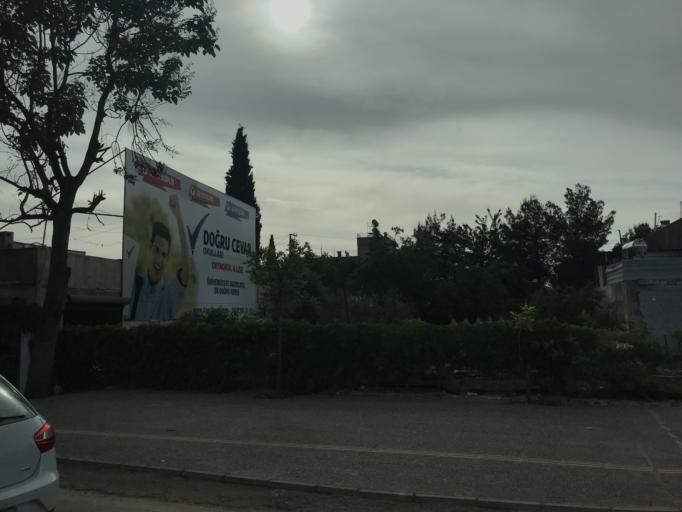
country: TR
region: Gaziantep
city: Sahinbey
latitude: 37.0610
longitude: 37.3337
